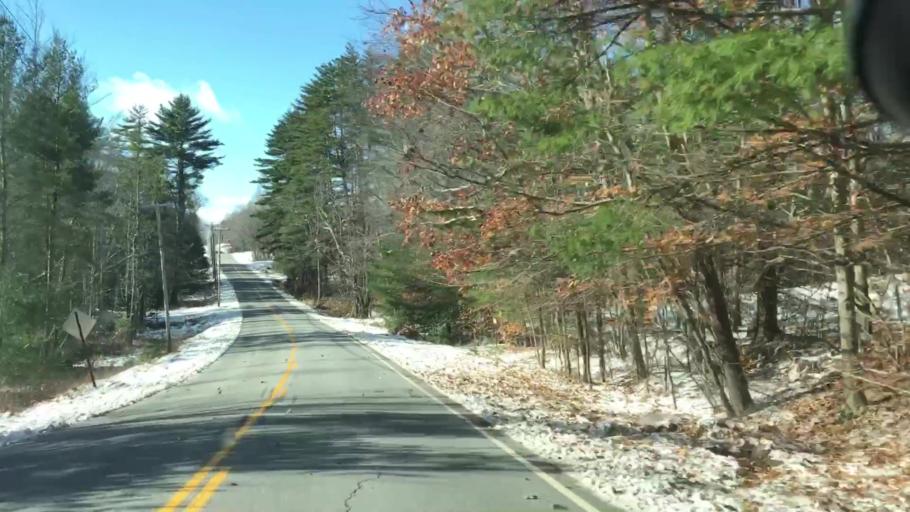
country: US
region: Maine
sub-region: Oxford County
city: Denmark
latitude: 43.9669
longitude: -70.8346
